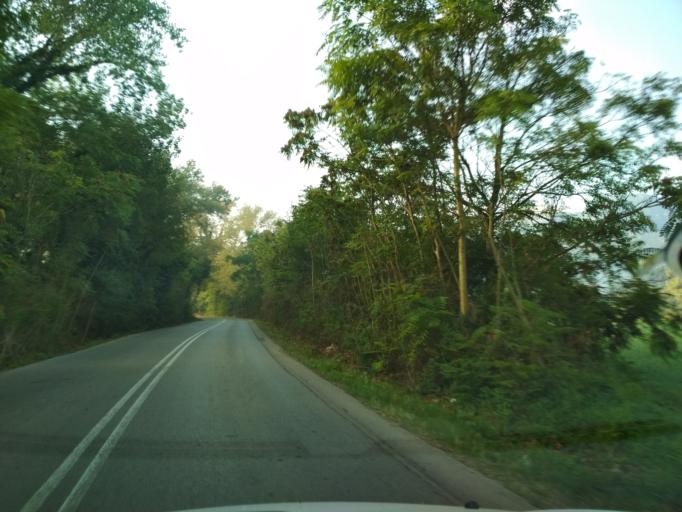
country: GR
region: Central Greece
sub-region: Nomos Evvoias
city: Prokopion
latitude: 38.7442
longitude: 23.4891
